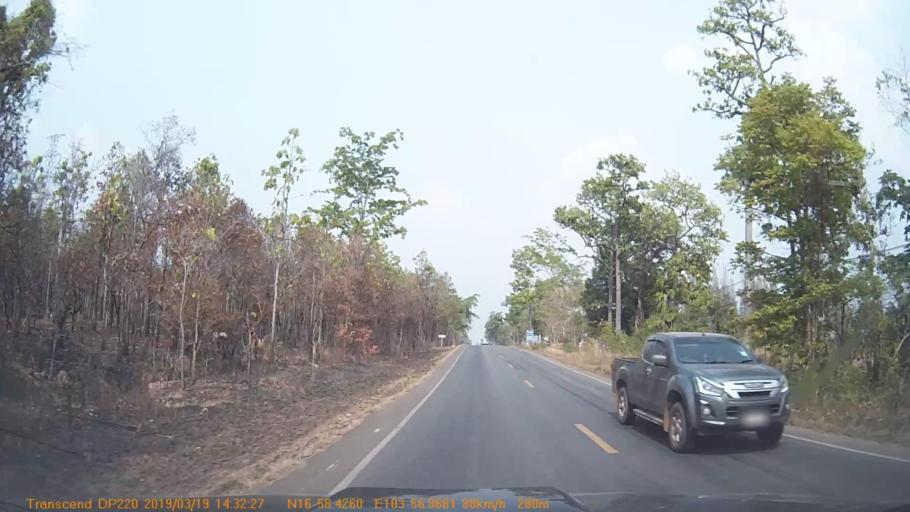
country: TH
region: Sakon Nakhon
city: Phu Phan
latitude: 16.9741
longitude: 103.9483
